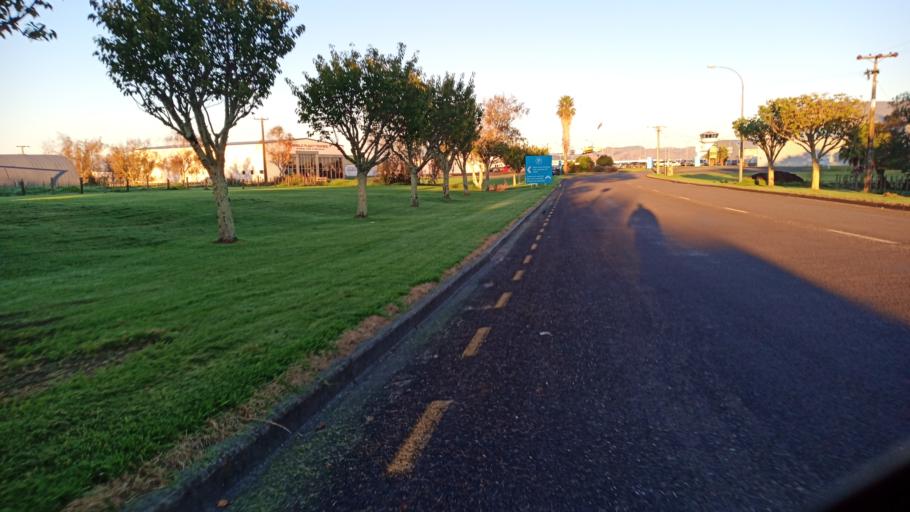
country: NZ
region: Gisborne
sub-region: Gisborne District
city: Gisborne
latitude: -38.6611
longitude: 177.9855
